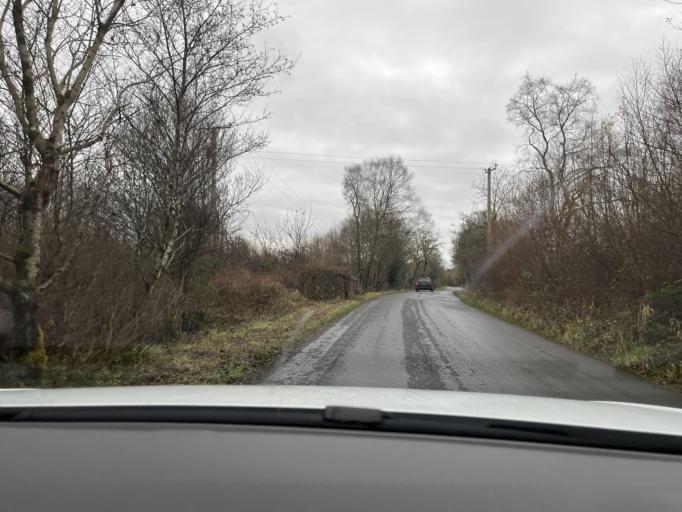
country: IE
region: Connaught
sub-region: County Leitrim
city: Manorhamilton
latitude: 54.2657
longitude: -8.2265
